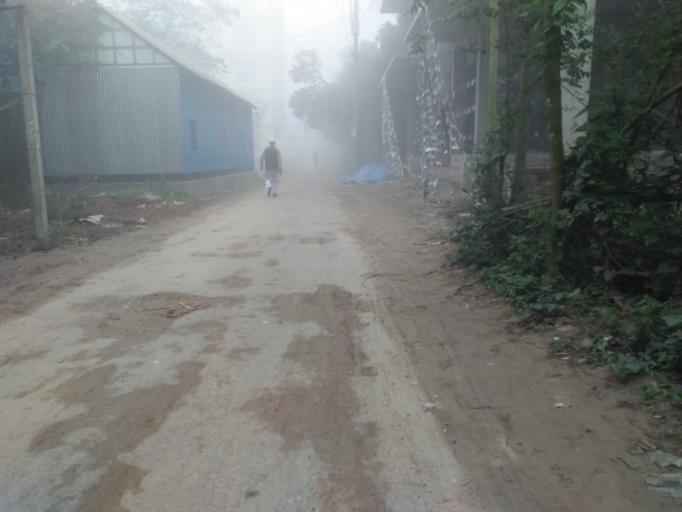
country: BD
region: Dhaka
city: Azimpur
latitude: 23.6880
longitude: 90.3033
